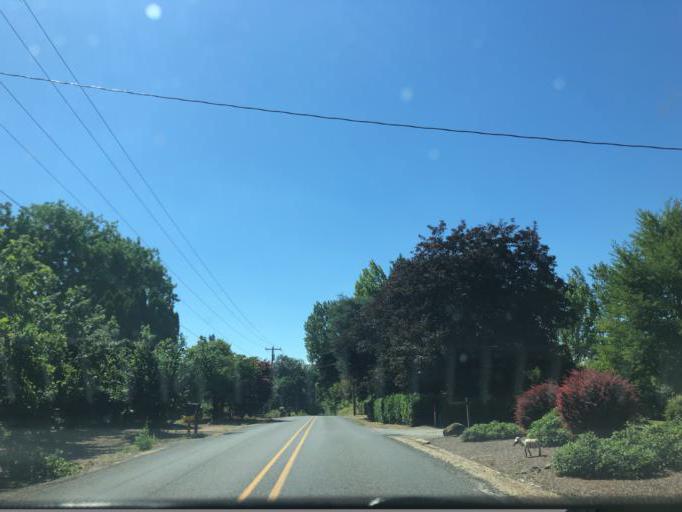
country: US
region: Oregon
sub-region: Marion County
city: Hubbard
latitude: 45.1733
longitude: -122.7335
